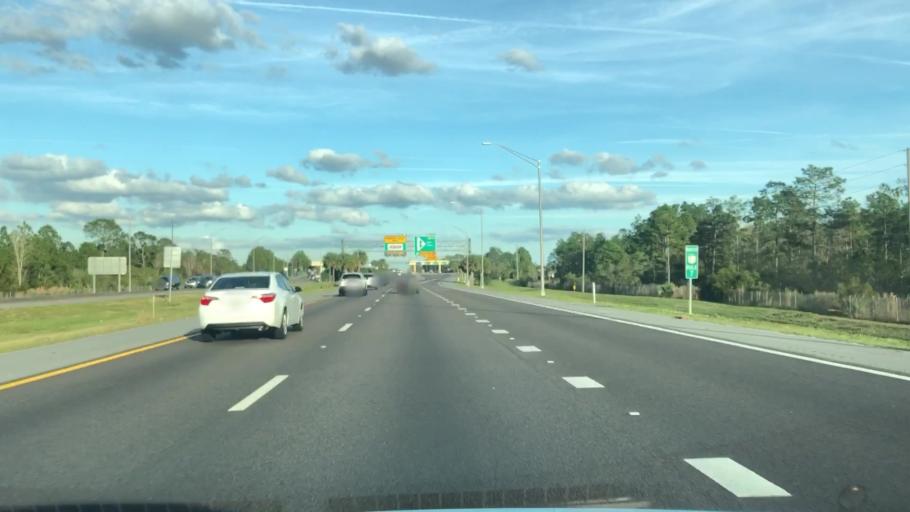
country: US
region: Florida
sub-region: Orange County
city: Hunters Creek
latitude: 28.3542
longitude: -81.4651
